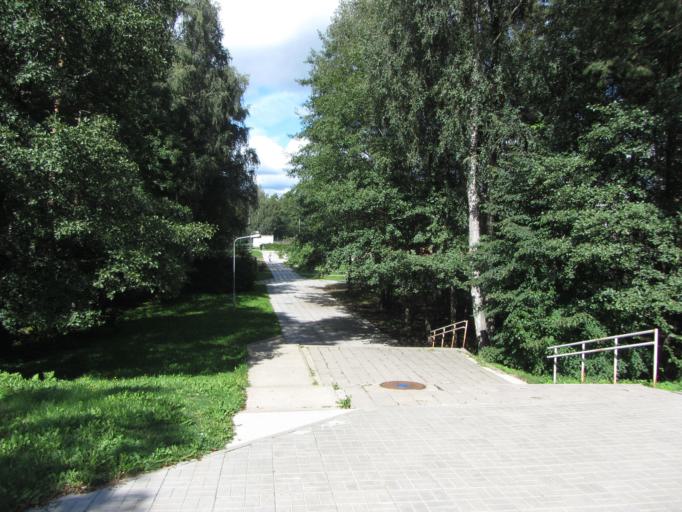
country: LT
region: Utenos apskritis
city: Visaginas
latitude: 55.6004
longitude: 26.4295
